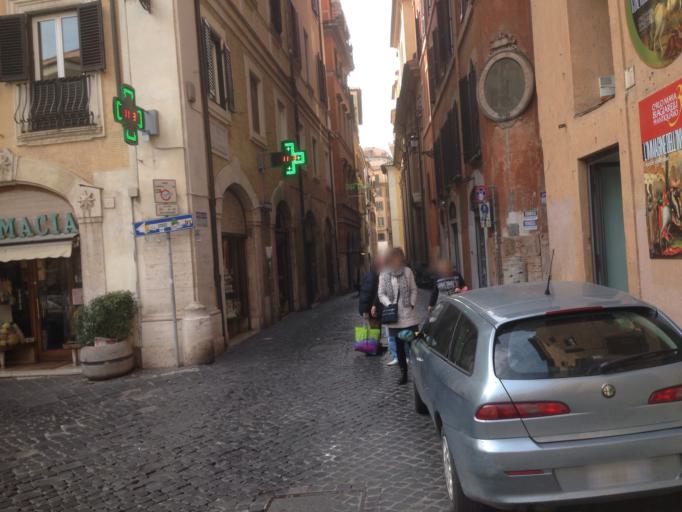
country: VA
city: Vatican City
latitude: 41.9001
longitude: 12.4777
